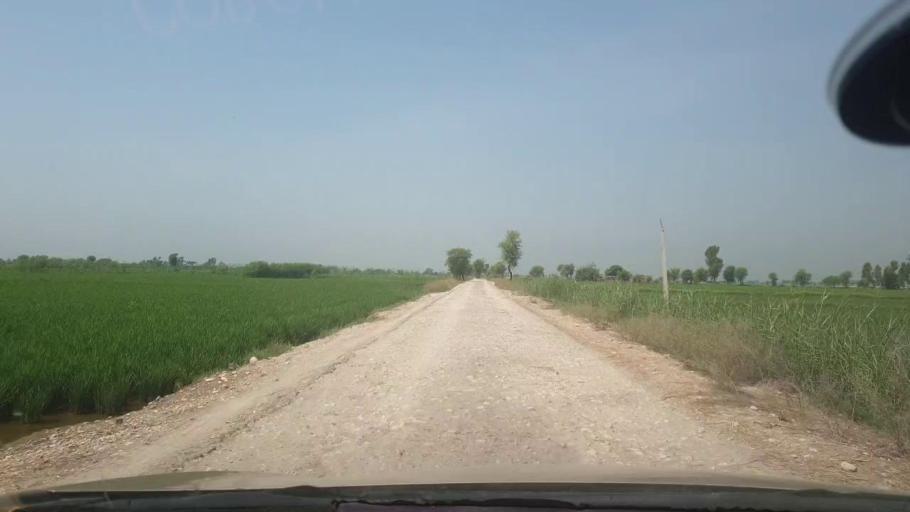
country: PK
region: Sindh
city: Shahdadkot
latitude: 27.7569
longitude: 67.9480
